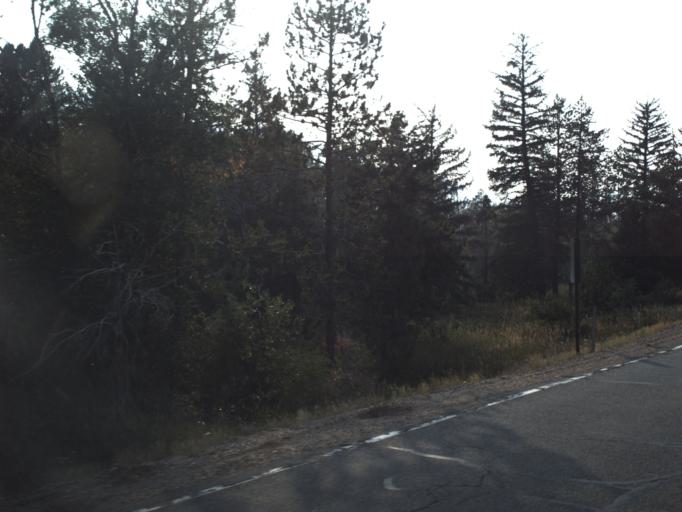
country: US
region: Utah
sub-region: Summit County
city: Francis
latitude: 40.6222
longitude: -111.1381
